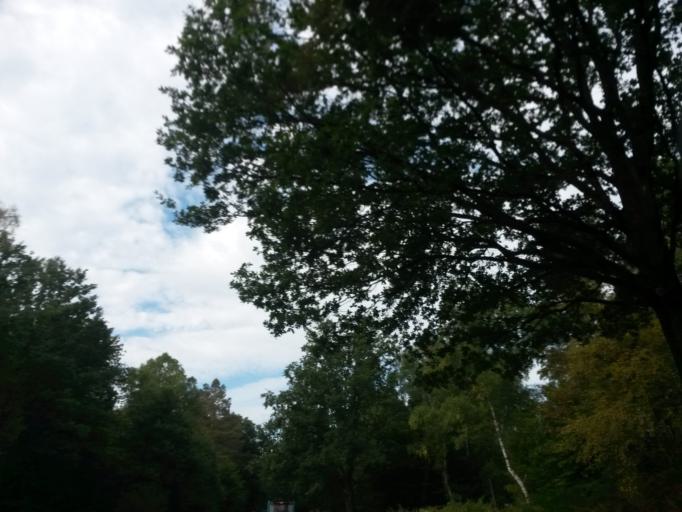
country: DE
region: North Rhine-Westphalia
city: Lohmar
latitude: 50.8445
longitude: 7.1860
